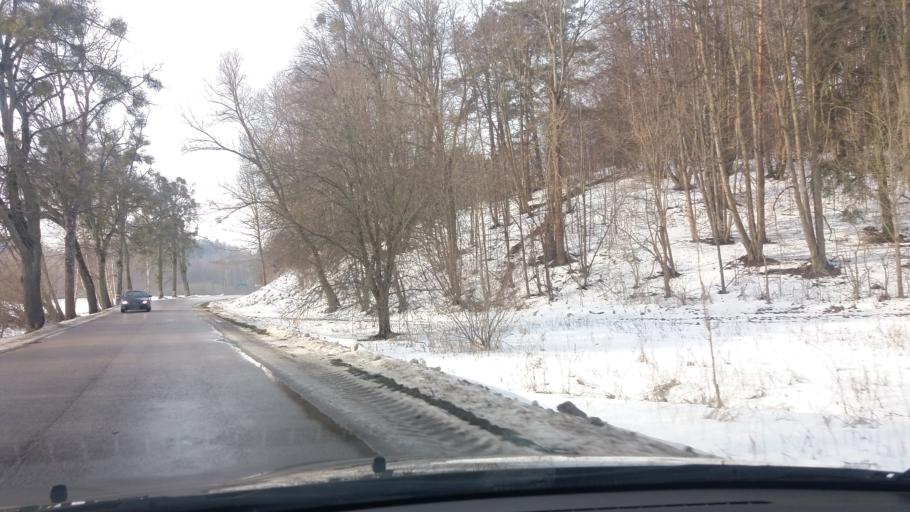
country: PL
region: Warmian-Masurian Voivodeship
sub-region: Powiat lidzbarski
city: Lidzbark Warminski
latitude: 54.1144
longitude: 20.6114
